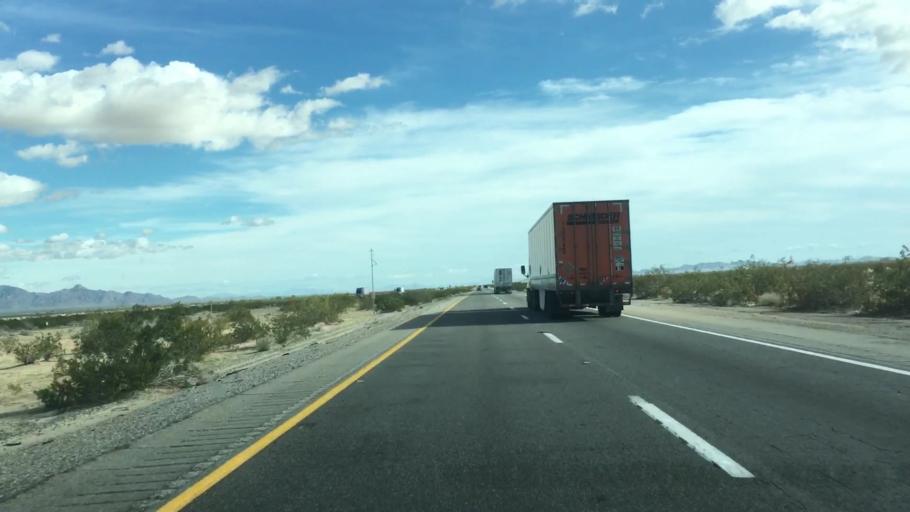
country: US
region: California
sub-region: Riverside County
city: Mesa Verde
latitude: 33.6285
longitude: -115.0665
